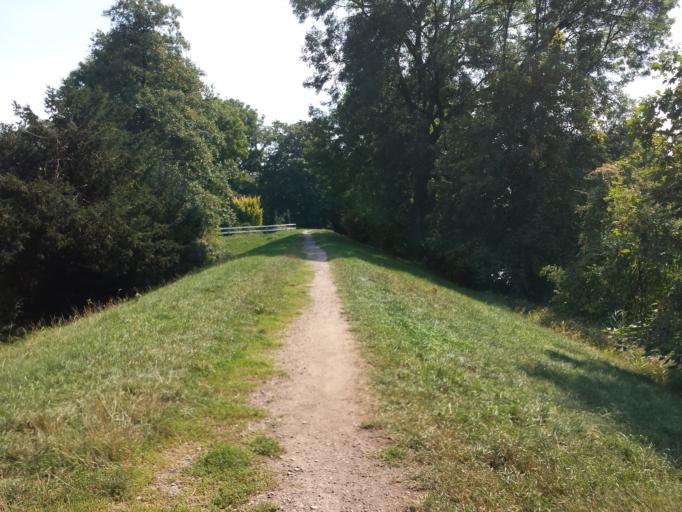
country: DE
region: Bremen
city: Bremen
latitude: 53.0259
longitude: 8.8164
